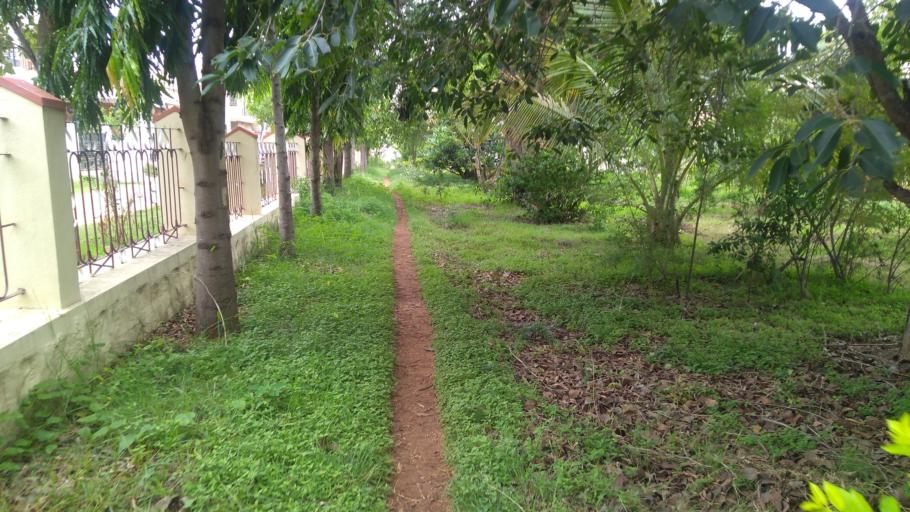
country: IN
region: Karnataka
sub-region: Mysore
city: Mysore
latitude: 12.2997
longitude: 76.6001
